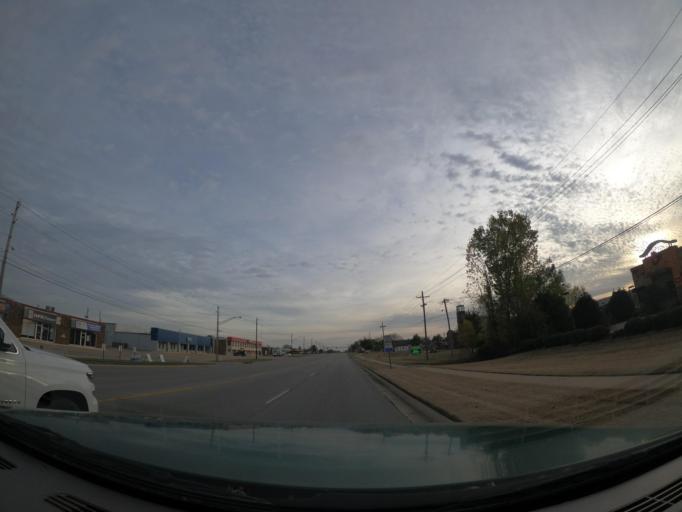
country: US
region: Oklahoma
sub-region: Tulsa County
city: Broken Arrow
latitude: 36.0572
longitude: -95.8154
